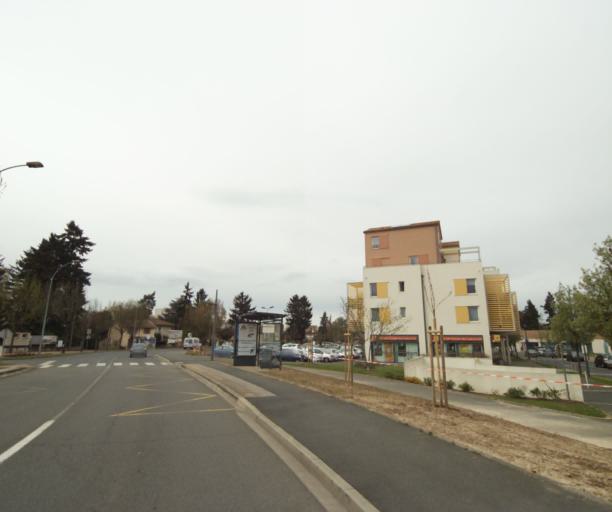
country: FR
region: Bourgogne
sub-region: Departement de Saone-et-Loire
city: Macon
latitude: 46.3087
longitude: 4.8122
